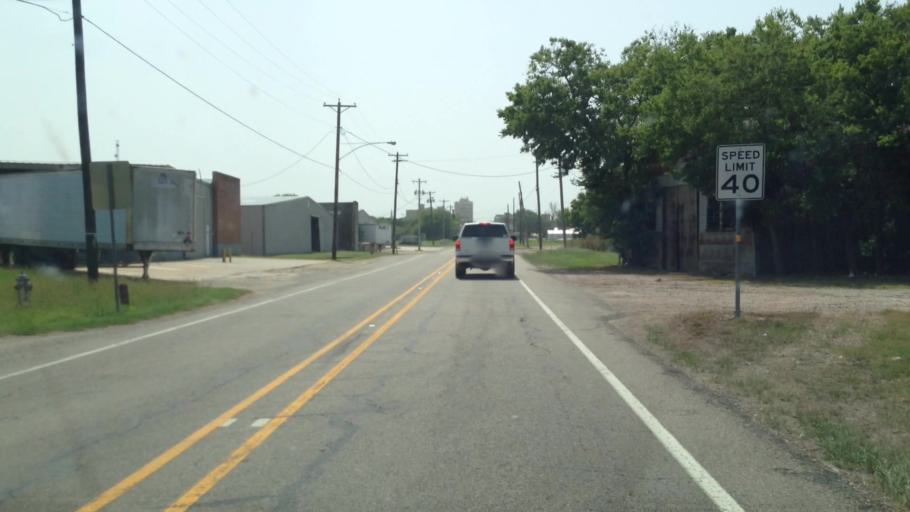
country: US
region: Texas
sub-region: Hunt County
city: Greenville
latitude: 33.1397
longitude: -96.0977
